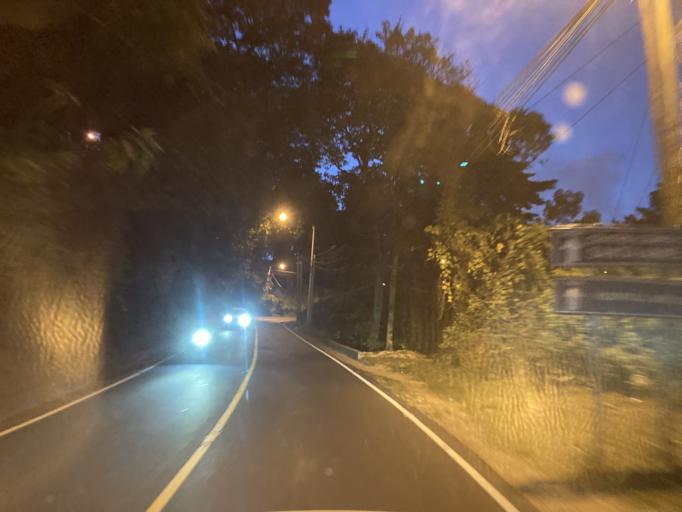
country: GT
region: Guatemala
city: Santa Catarina Pinula
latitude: 14.5976
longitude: -90.4660
